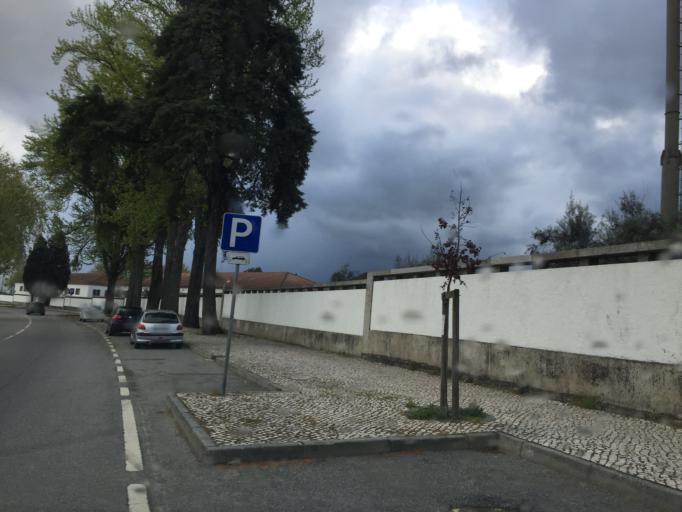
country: PT
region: Viseu
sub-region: Viseu
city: Viseu
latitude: 40.6462
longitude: -7.9224
